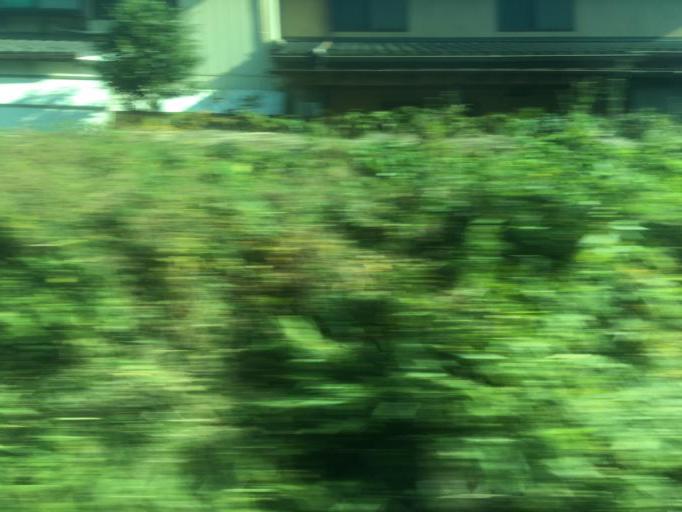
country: JP
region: Ibaraki
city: Ishioka
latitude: 36.1524
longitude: 140.2877
